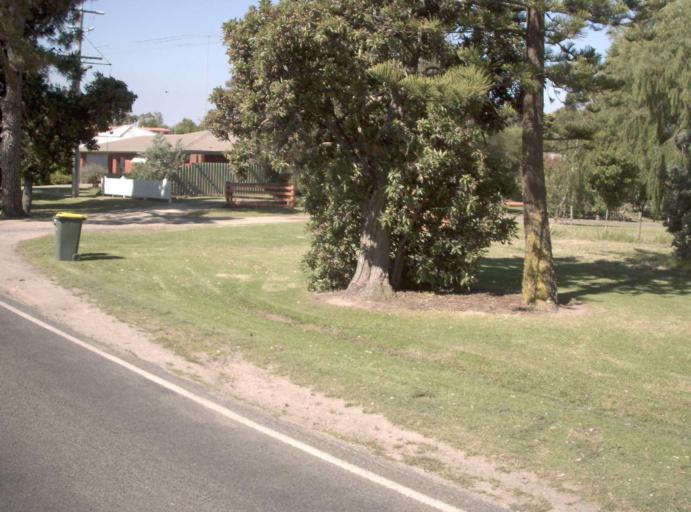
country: AU
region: Victoria
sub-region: Latrobe
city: Traralgon
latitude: -38.5714
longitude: 146.6742
